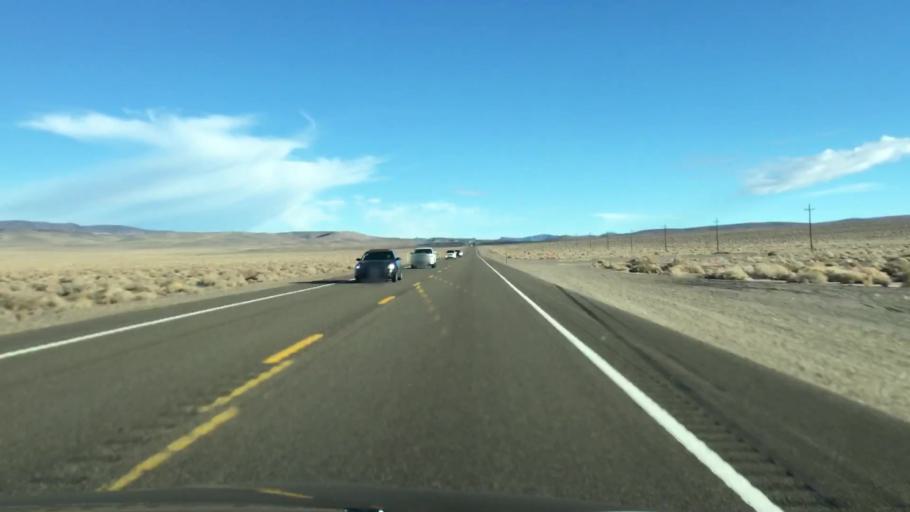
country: US
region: Nevada
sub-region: Mineral County
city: Hawthorne
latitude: 38.2540
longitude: -118.0811
